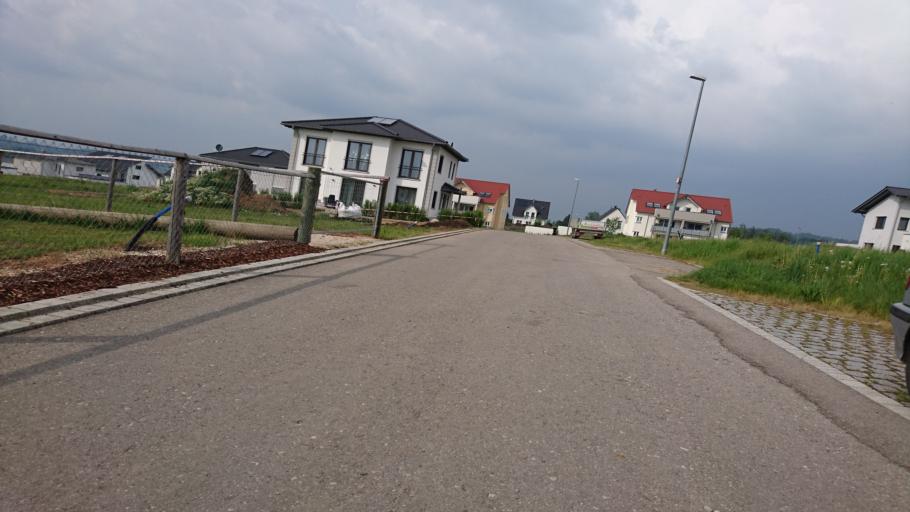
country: DE
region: Bavaria
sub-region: Swabia
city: Diedorf
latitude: 48.3572
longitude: 10.7871
